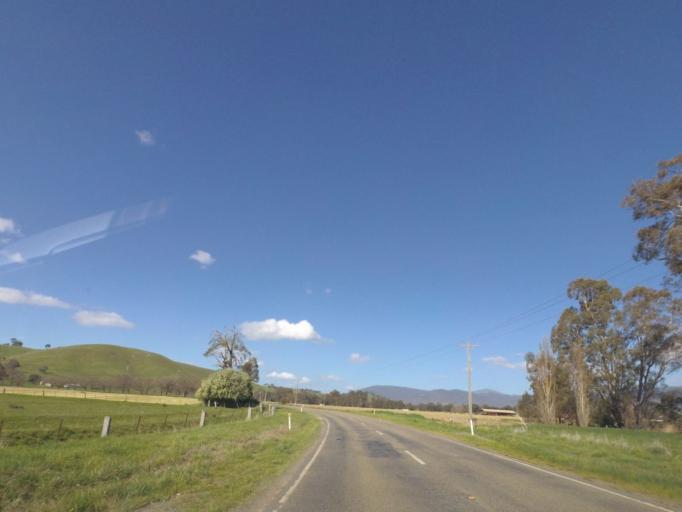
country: AU
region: Victoria
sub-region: Murrindindi
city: Alexandra
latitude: -37.2277
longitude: 145.7528
